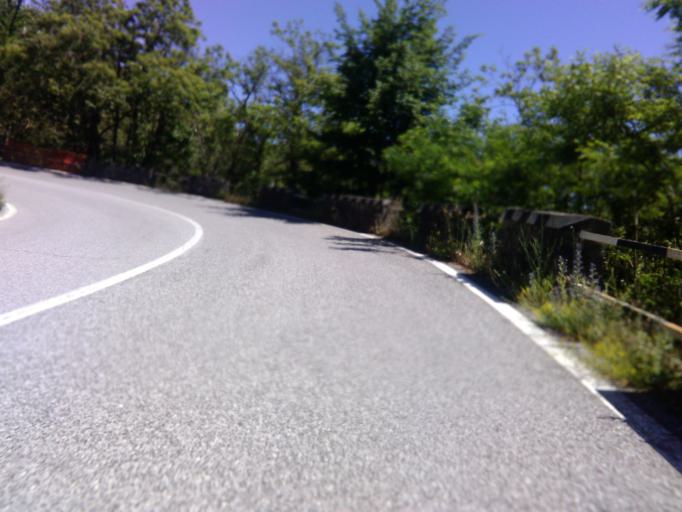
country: IT
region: Tuscany
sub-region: Provincia di Massa-Carrara
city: Pontremoli
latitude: 44.4046
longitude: 9.8850
